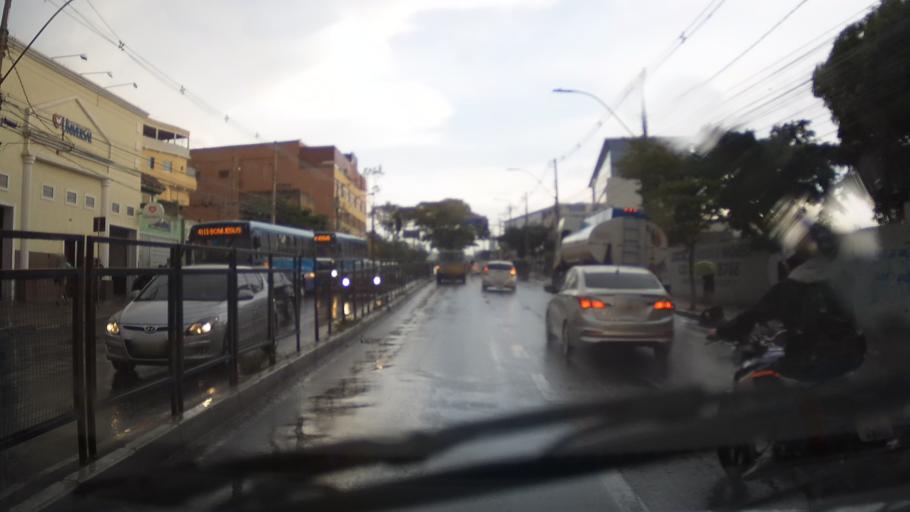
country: BR
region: Minas Gerais
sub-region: Belo Horizonte
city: Belo Horizonte
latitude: -19.9515
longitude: -43.9608
